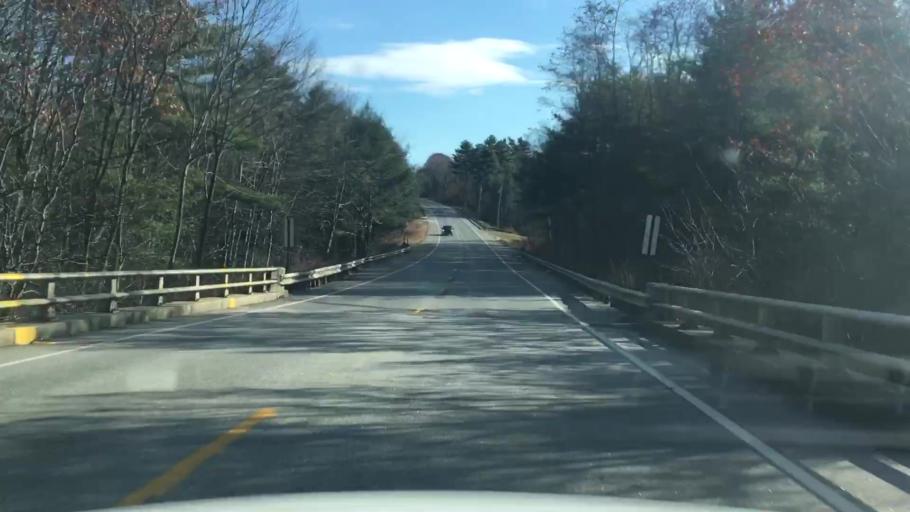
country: US
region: Maine
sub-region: Kennebec County
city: Windsor
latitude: 44.2582
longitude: -69.5536
